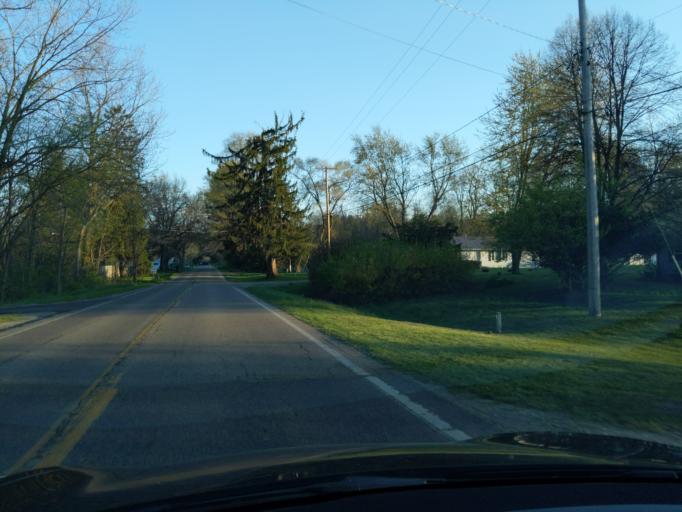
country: US
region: Michigan
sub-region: Jackson County
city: Jackson
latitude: 42.2678
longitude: -84.4832
